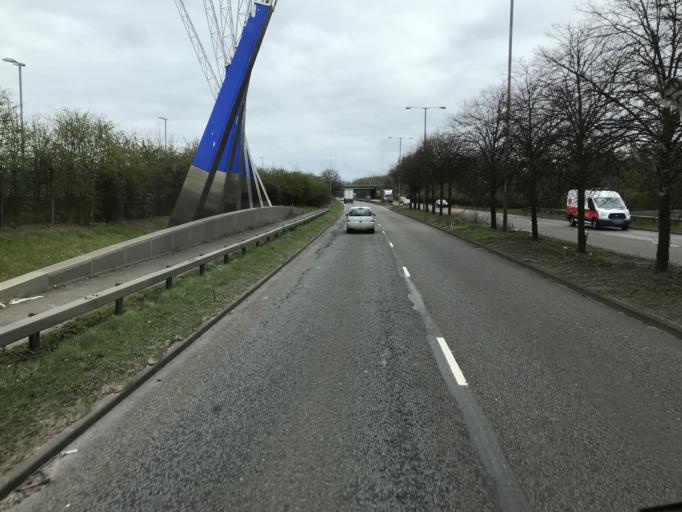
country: GB
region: England
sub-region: Borough of Halton
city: Hale
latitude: 53.3477
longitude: -2.8245
